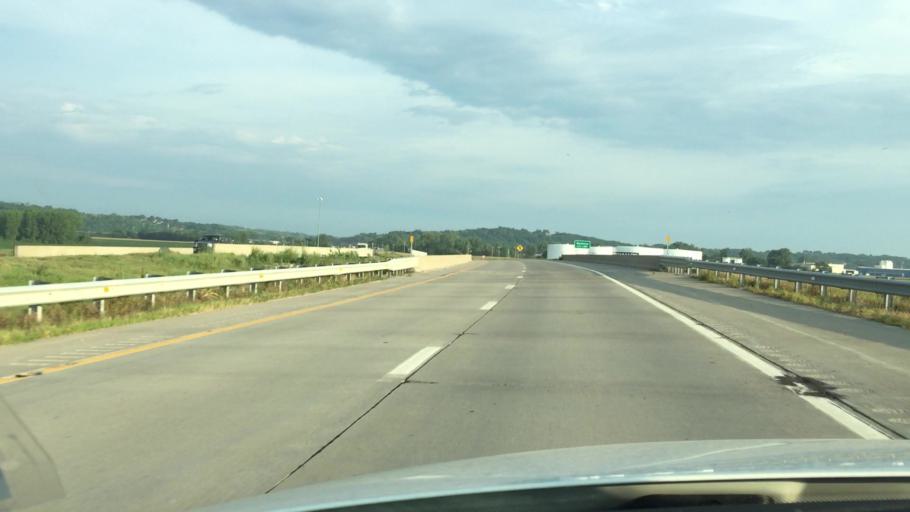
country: US
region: Kansas
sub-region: Doniphan County
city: Wathena
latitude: 39.7468
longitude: -94.9241
